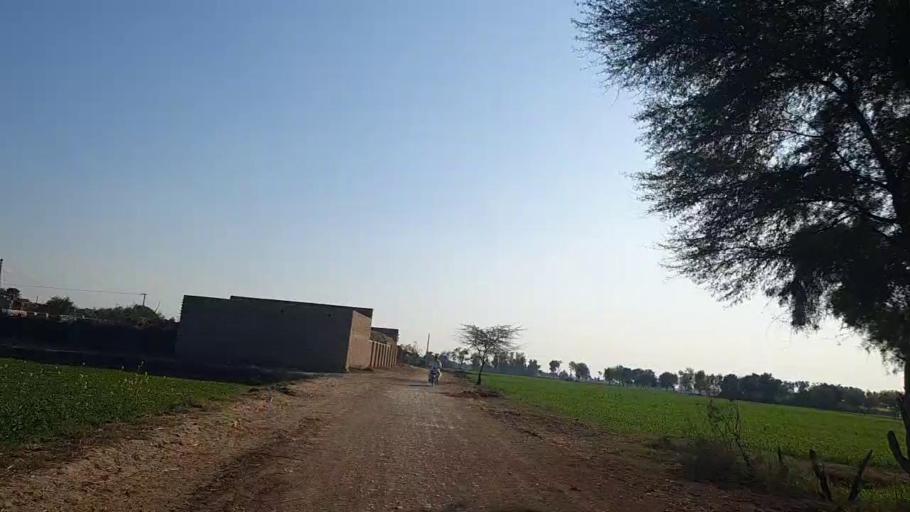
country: PK
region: Sindh
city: Sakrand
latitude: 26.3123
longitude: 68.1819
